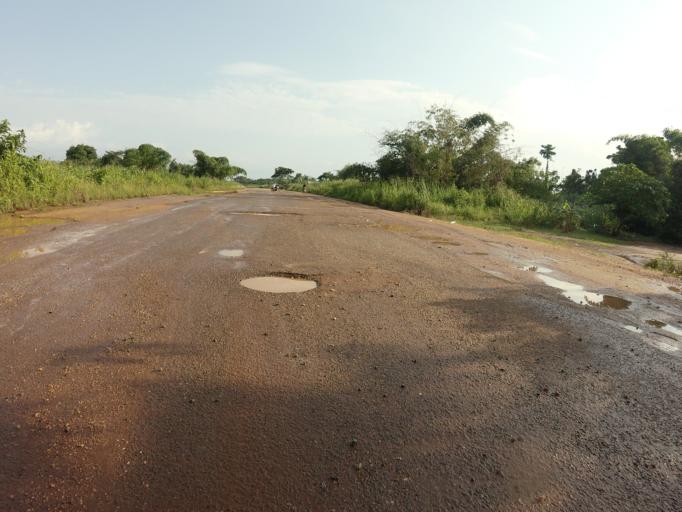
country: GH
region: Volta
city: Hohoe
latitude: 7.0733
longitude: 0.4363
